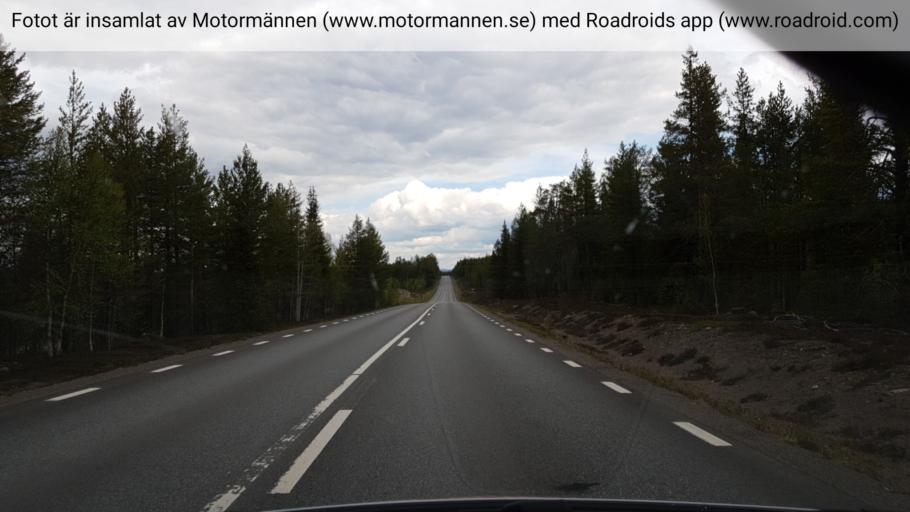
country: SE
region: Norrbotten
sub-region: Arvidsjaurs Kommun
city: Arvidsjaur
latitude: 65.5348
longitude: 19.2386
